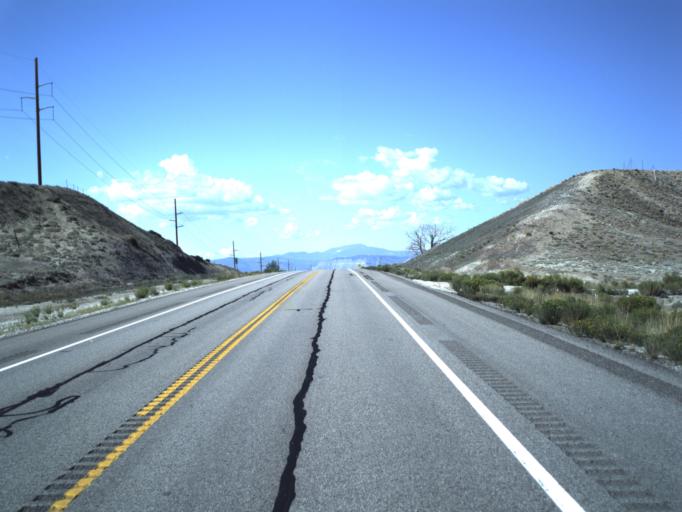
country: US
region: Utah
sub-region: Emery County
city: Ferron
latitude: 38.9351
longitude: -111.2284
